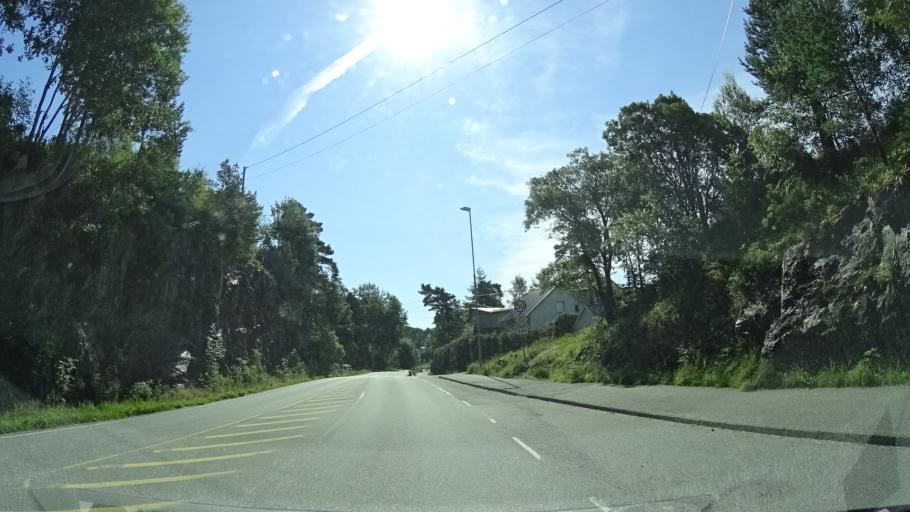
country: NO
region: Hordaland
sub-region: Stord
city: Sagvag
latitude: 59.7747
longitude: 5.3955
